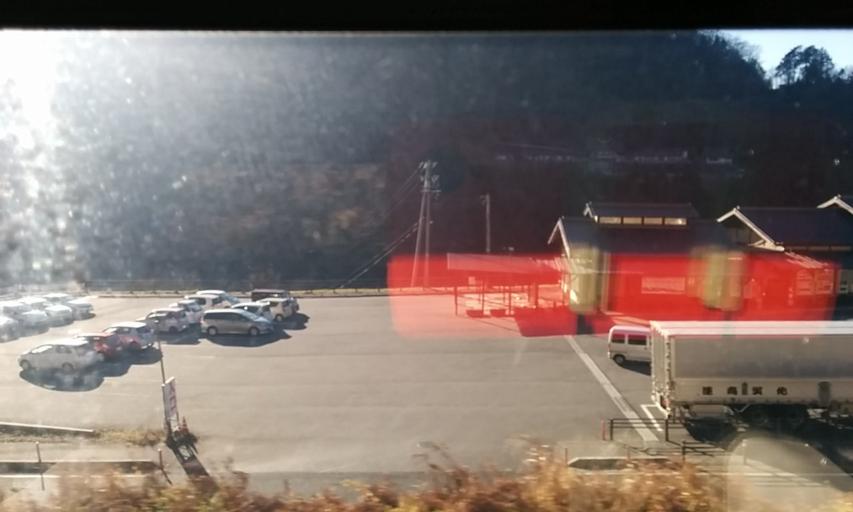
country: JP
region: Nagano
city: Ina
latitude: 35.8169
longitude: 137.6831
